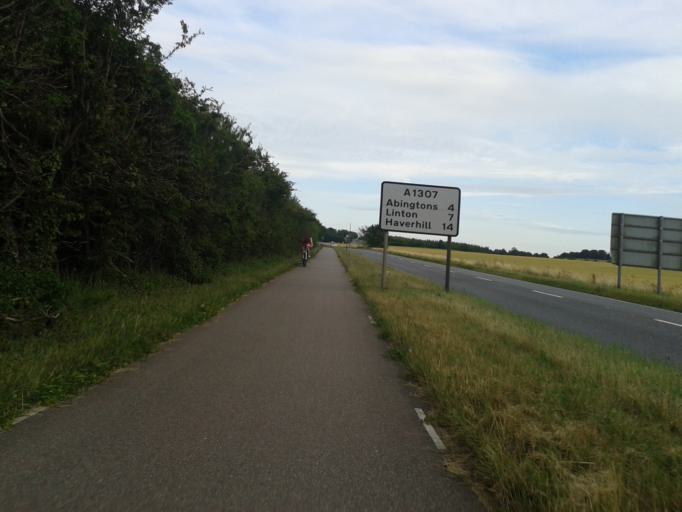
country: GB
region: England
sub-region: Cambridgeshire
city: Sawston
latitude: 52.1638
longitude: 0.1651
